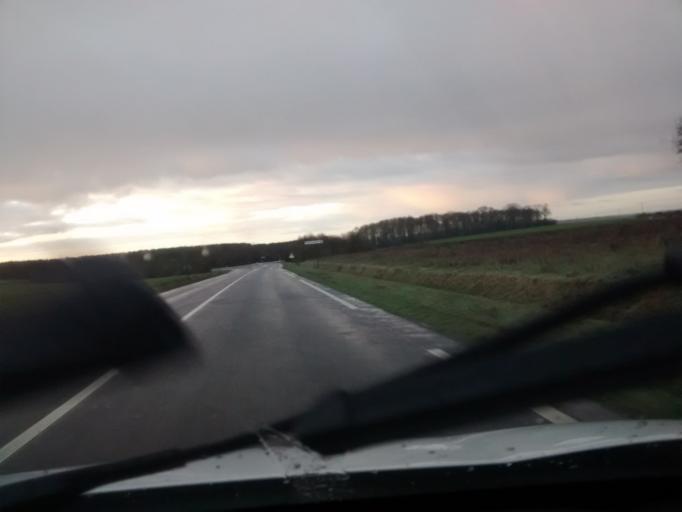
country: FR
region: Brittany
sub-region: Departement d'Ille-et-Vilaine
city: Louvigne-de-Bais
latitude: 48.0319
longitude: -1.3156
